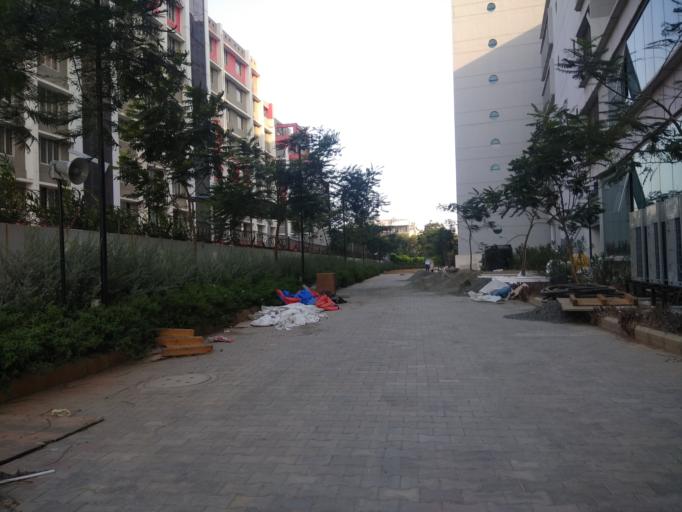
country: IN
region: Tamil Nadu
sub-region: Chennai
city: Gandhi Nagar
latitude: 12.9910
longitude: 80.2436
